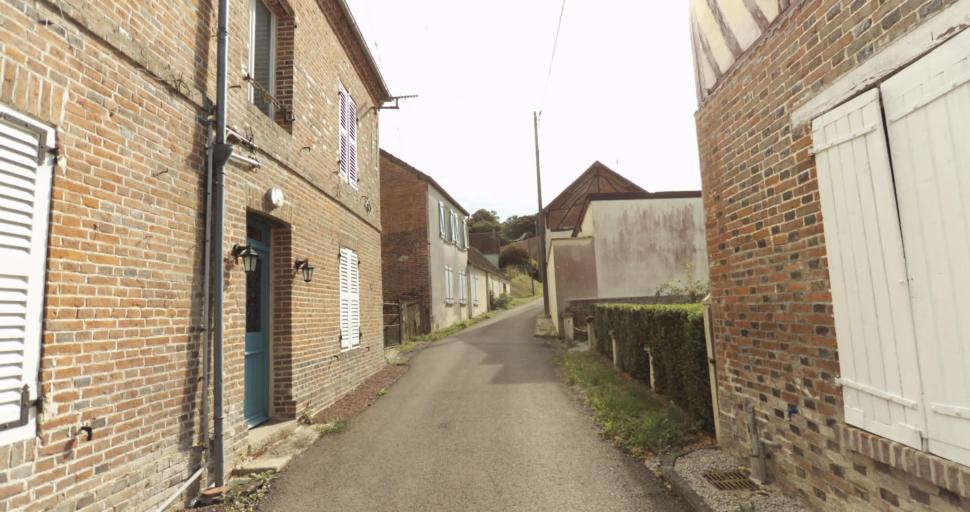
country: FR
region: Lower Normandy
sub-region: Departement de l'Orne
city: Gace
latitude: 48.8138
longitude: 0.2243
